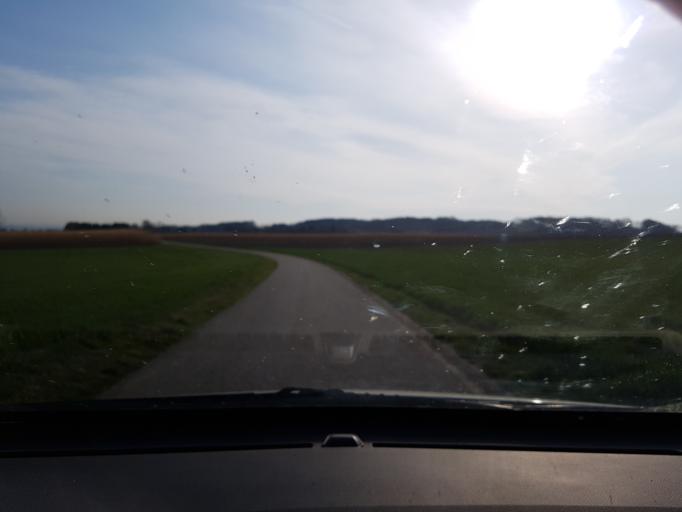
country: AT
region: Upper Austria
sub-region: Politischer Bezirk Linz-Land
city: Sankt Florian
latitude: 48.1965
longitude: 14.3722
